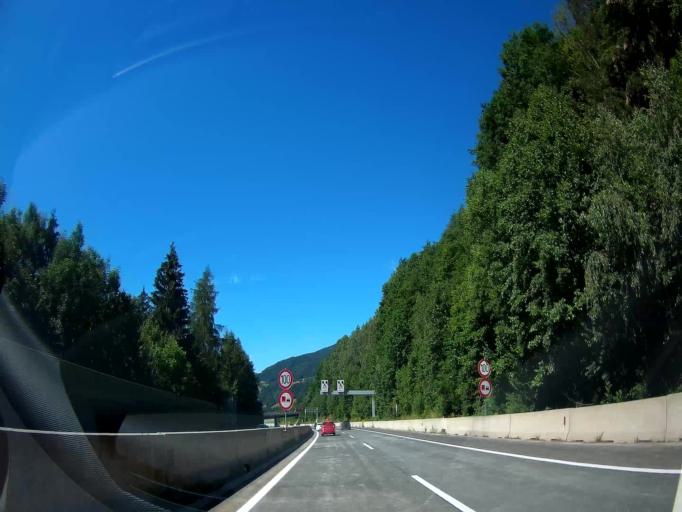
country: AT
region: Carinthia
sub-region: Politischer Bezirk Spittal an der Drau
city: Trebesing
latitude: 46.8934
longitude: 13.5224
